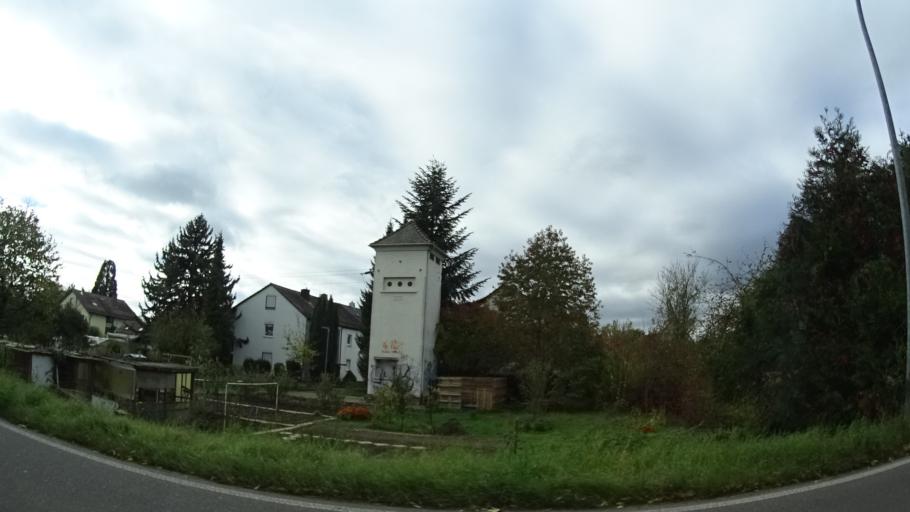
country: DE
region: Baden-Wuerttemberg
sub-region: Karlsruhe Region
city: Weingarten
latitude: 49.0647
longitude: 8.5141
